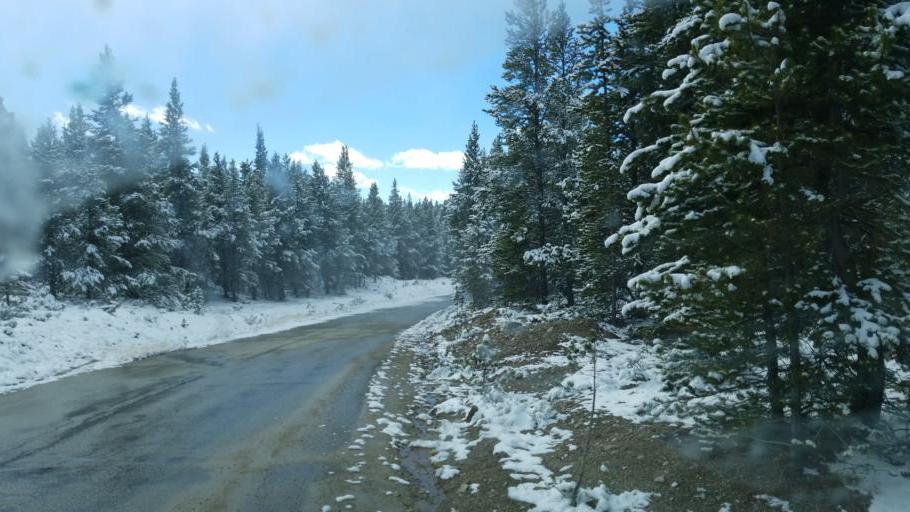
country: US
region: Colorado
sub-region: Lake County
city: Leadville
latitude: 39.2561
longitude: -106.2665
